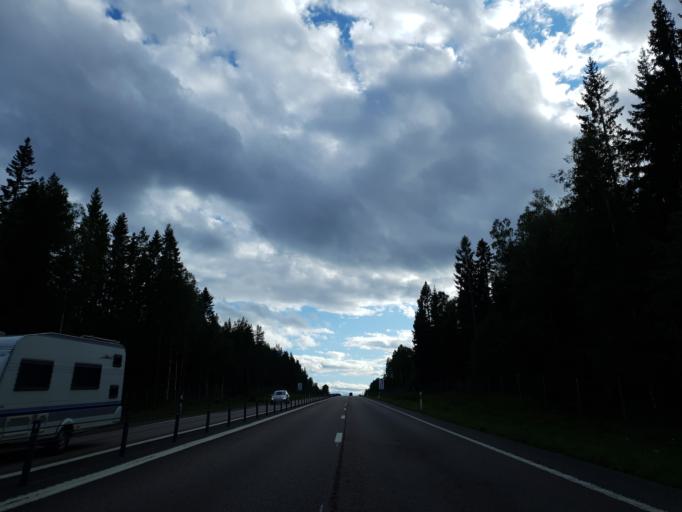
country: SE
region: Vaesternorrland
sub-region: Haernoesands Kommun
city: Haernoesand
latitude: 62.5725
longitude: 17.7449
